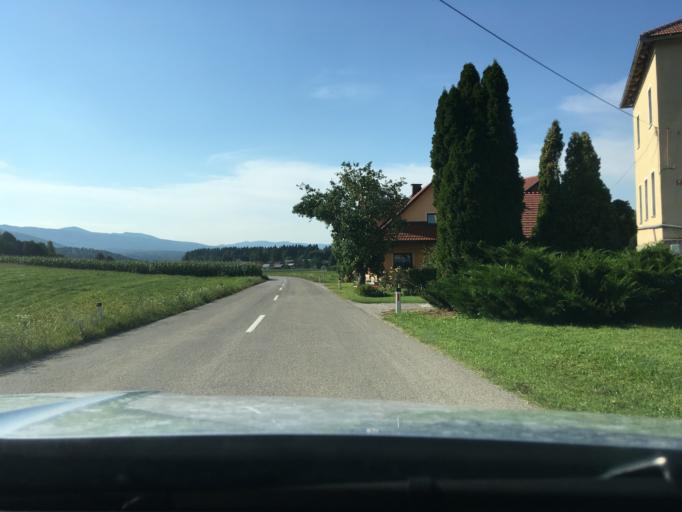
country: SI
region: Crnomelj
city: Crnomelj
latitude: 45.4788
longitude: 15.2084
